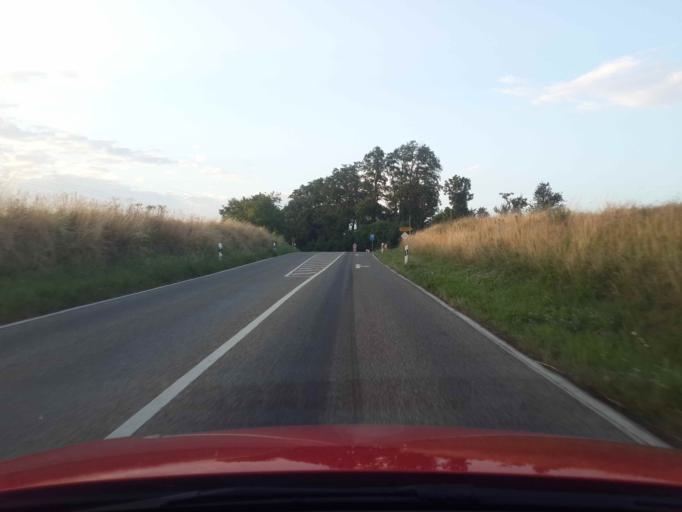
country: DE
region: Baden-Wuerttemberg
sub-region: Regierungsbezirk Stuttgart
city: Nordheim
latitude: 49.1239
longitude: 9.1304
